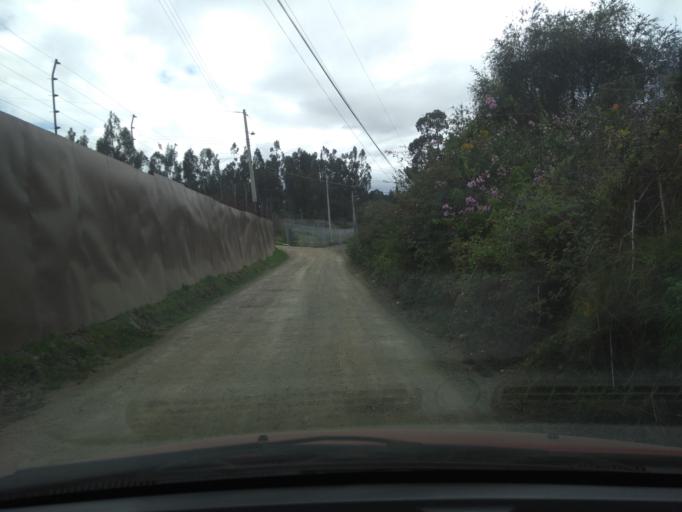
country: EC
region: Azuay
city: Llacao
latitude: -2.8528
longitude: -78.9170
